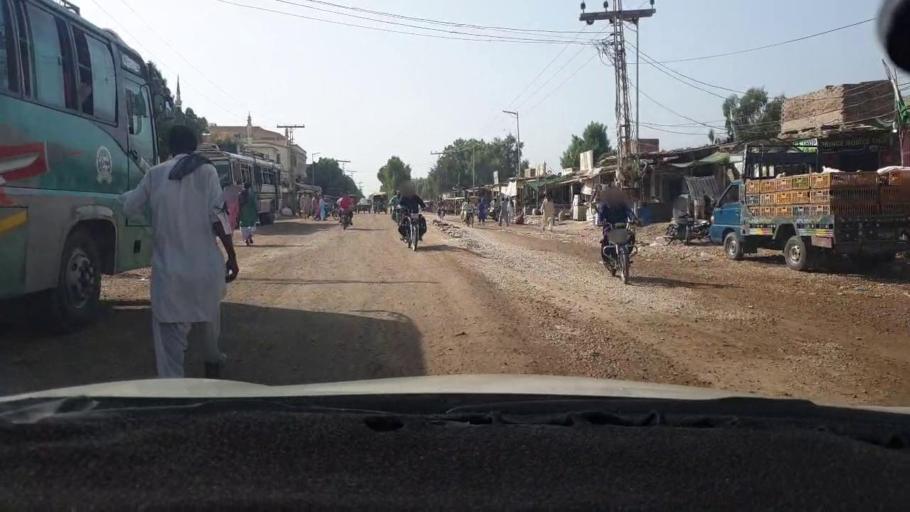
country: PK
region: Sindh
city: Sanghar
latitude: 26.0433
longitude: 68.9496
